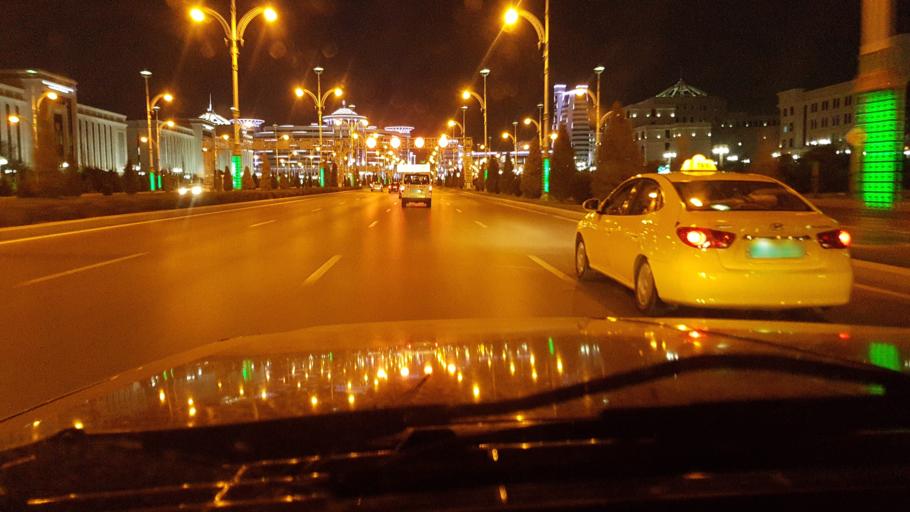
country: TM
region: Ahal
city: Ashgabat
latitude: 37.8979
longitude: 58.3645
